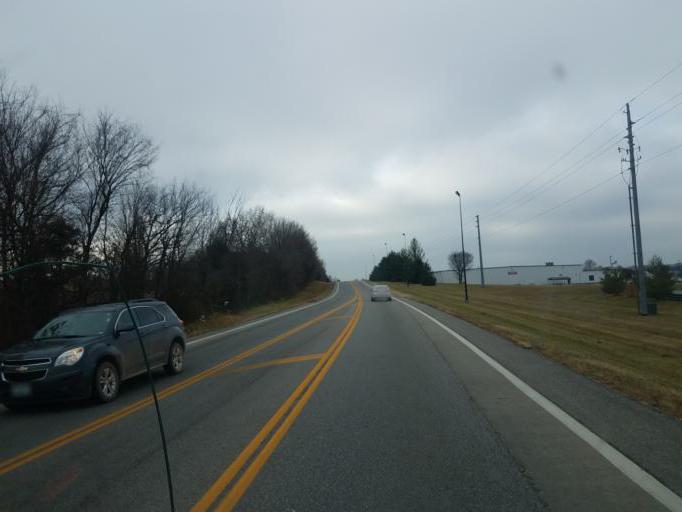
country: US
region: Missouri
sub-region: Greene County
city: Strafford
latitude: 37.2440
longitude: -93.1950
